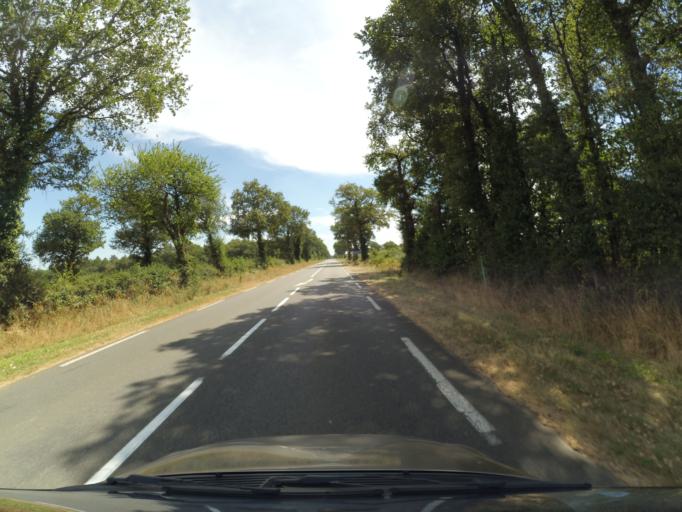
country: FR
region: Poitou-Charentes
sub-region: Departement de la Vienne
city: Availles-Limouzine
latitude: 46.0809
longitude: 0.5893
